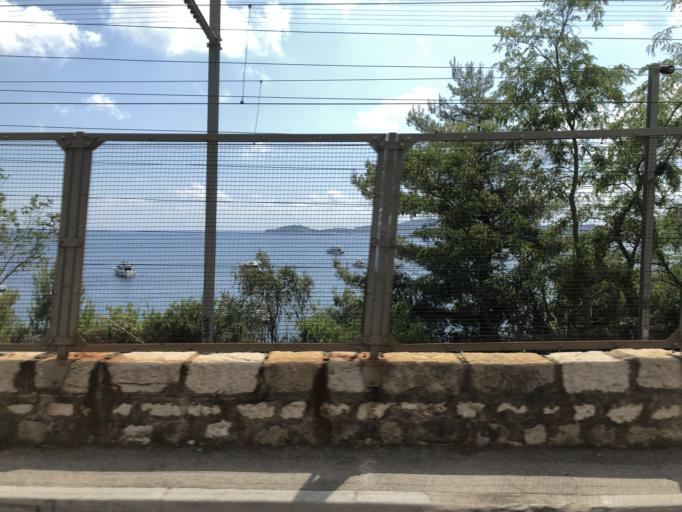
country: FR
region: Provence-Alpes-Cote d'Azur
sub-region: Departement des Alpes-Maritimes
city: Eze
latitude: 43.7225
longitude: 7.3647
